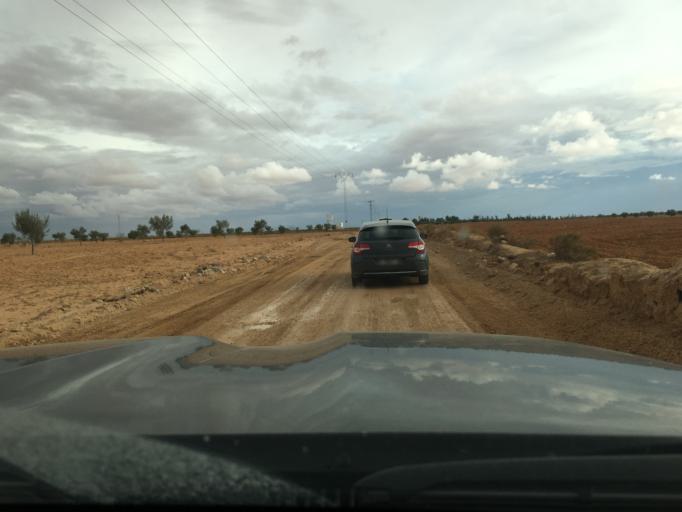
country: TN
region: Madanin
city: Medenine
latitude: 33.2787
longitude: 10.5575
